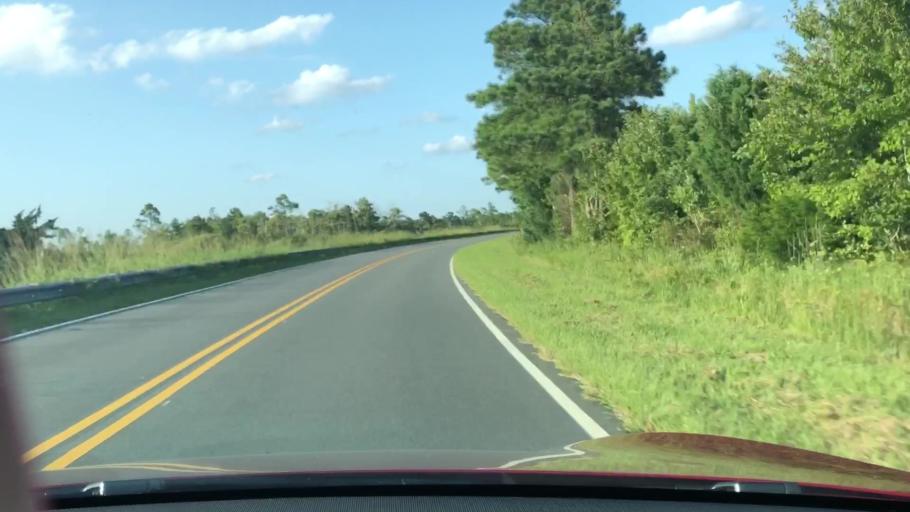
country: US
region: North Carolina
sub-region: Dare County
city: Wanchese
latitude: 35.6910
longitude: -75.7808
